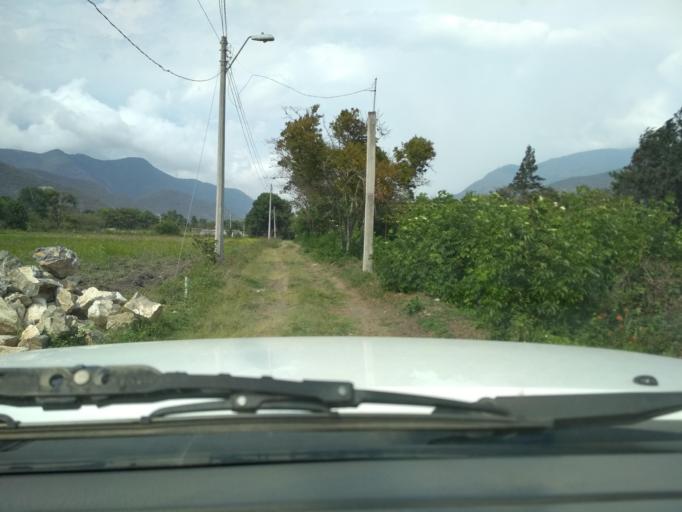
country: MX
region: Veracruz
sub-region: Acultzingo
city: Sierra de Agua
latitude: 18.7598
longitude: -97.2322
